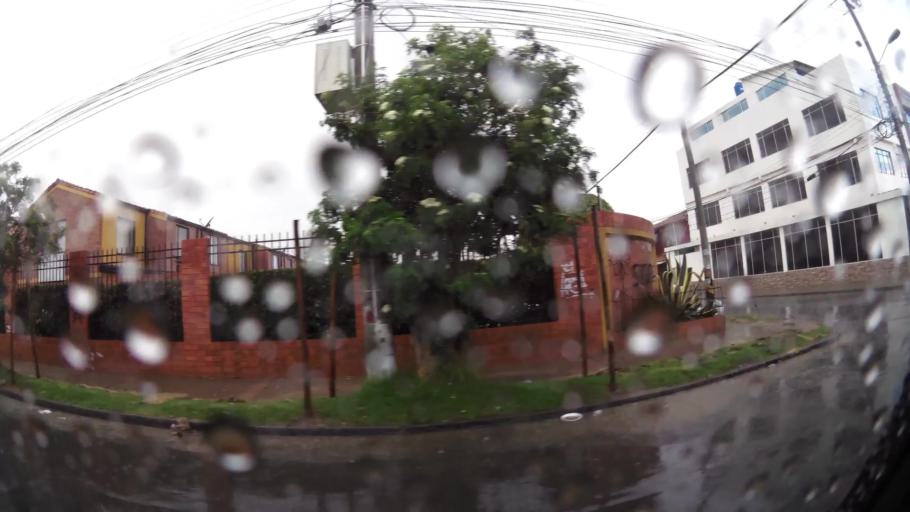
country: CO
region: Cundinamarca
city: Chia
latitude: 4.8627
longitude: -74.0645
